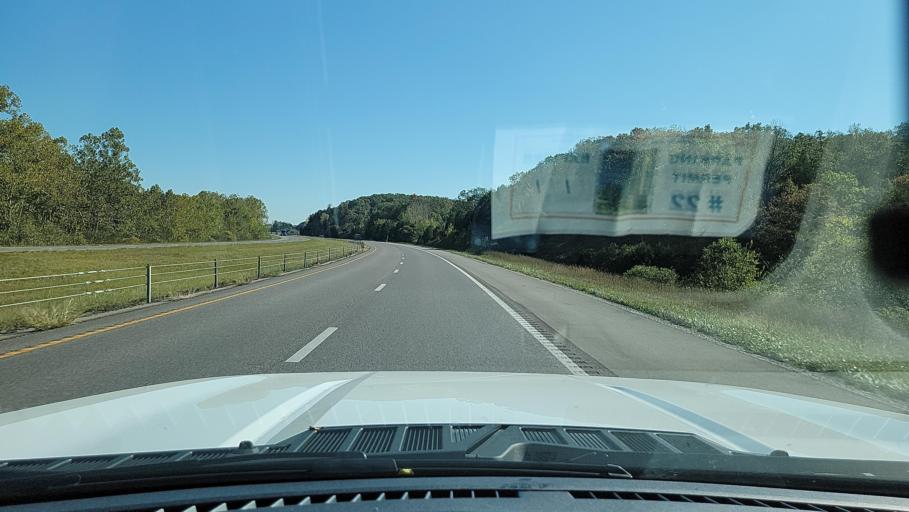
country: US
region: Missouri
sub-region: Jefferson County
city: Crystal City
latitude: 38.0730
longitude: -90.2928
